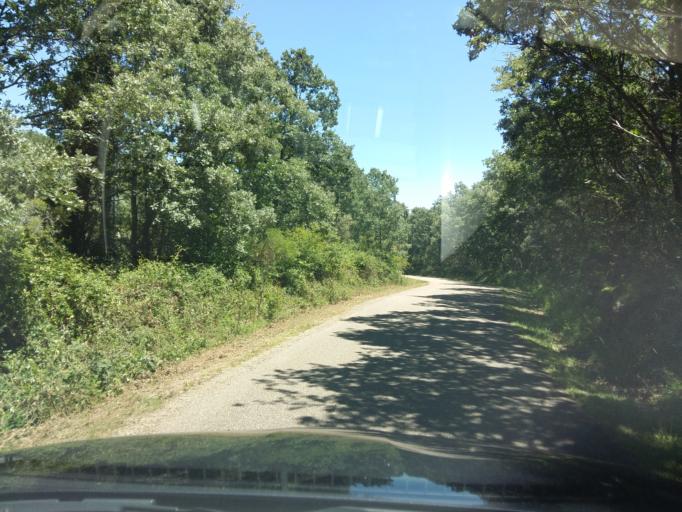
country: ES
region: Aragon
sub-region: Provincia de Zaragoza
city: Litago
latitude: 41.7857
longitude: -1.7717
